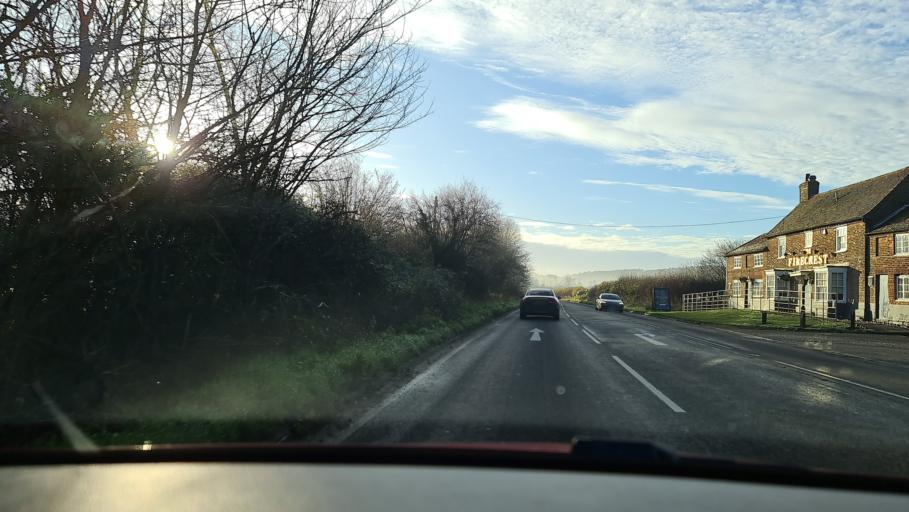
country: GB
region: England
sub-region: Buckinghamshire
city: Wendover
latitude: 51.7409
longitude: -0.7339
